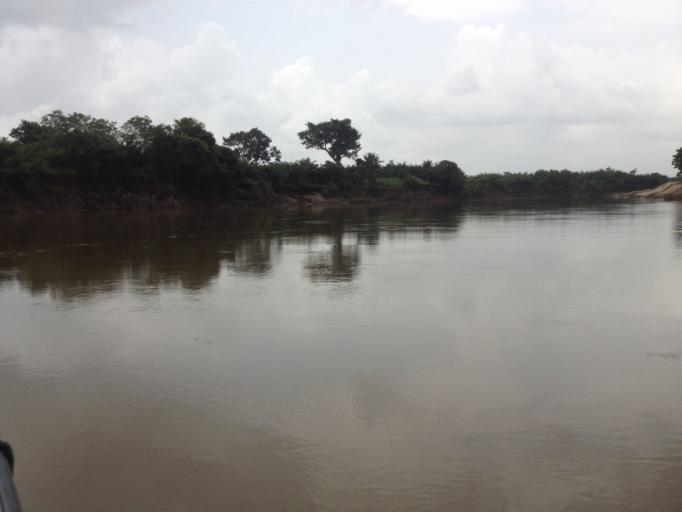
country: BJ
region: Mono
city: Lokossa
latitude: 6.5024
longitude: 1.6969
